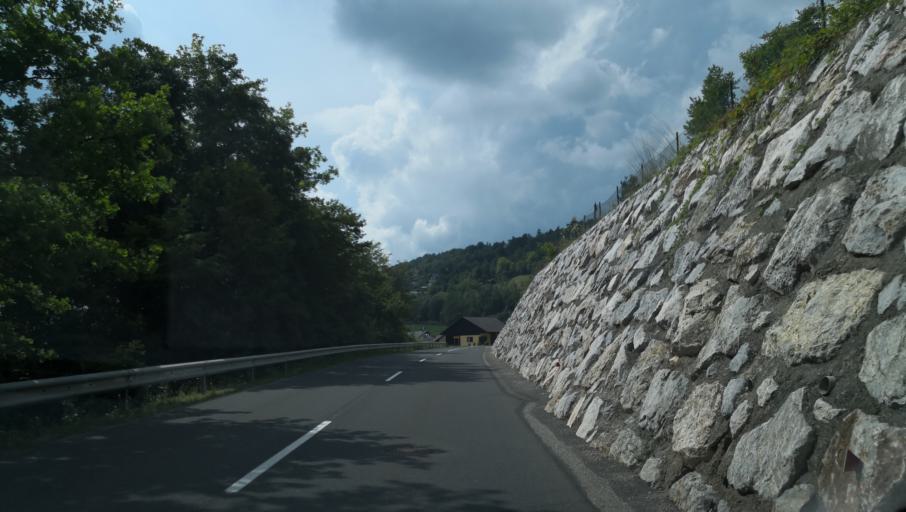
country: SI
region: Zuzemberk
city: Zuzemberk
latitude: 45.8550
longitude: 14.8843
